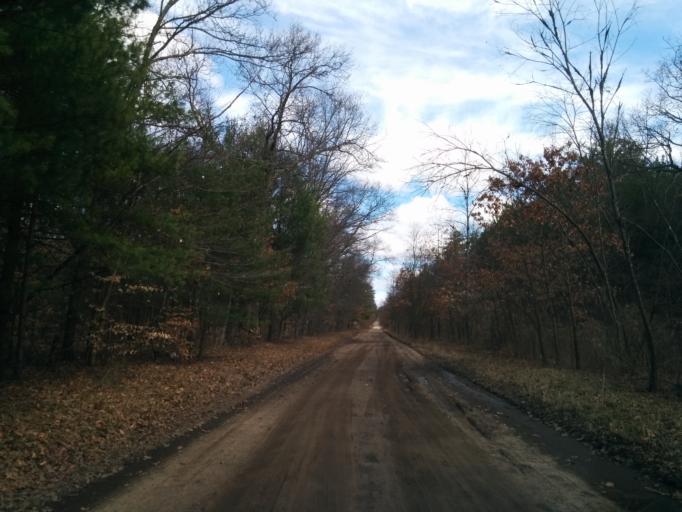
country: US
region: Michigan
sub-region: Newaygo County
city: Newaygo
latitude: 43.4223
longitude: -85.7275
